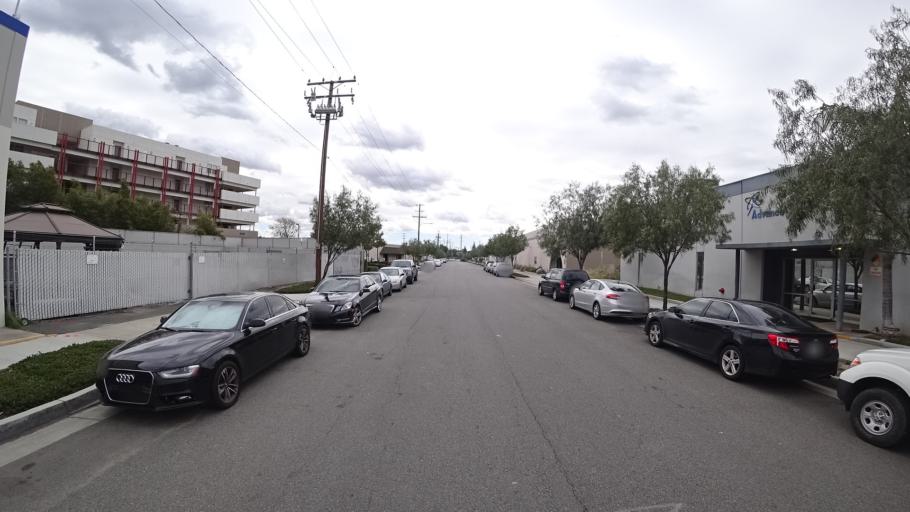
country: US
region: California
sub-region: Orange County
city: Placentia
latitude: 33.8540
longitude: -117.8424
